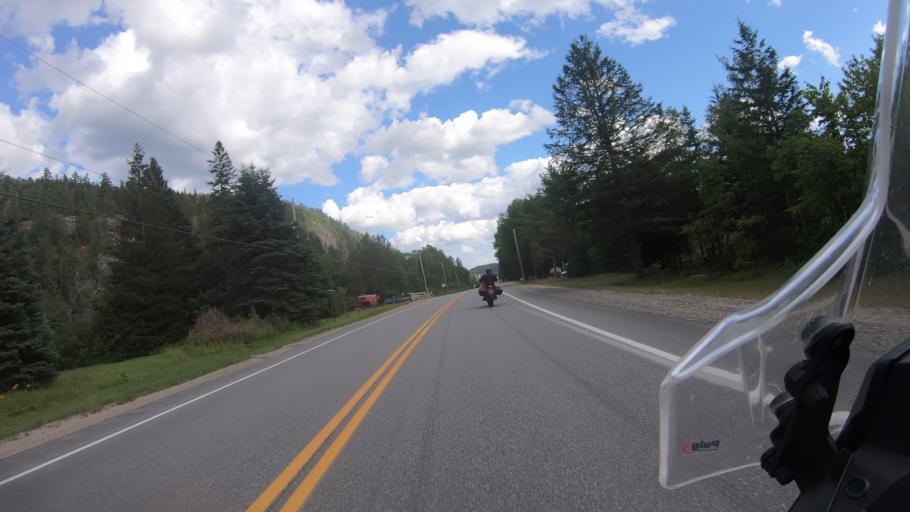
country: CA
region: Quebec
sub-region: Mauricie
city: Saint-Tite
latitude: 46.9928
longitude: -72.9154
